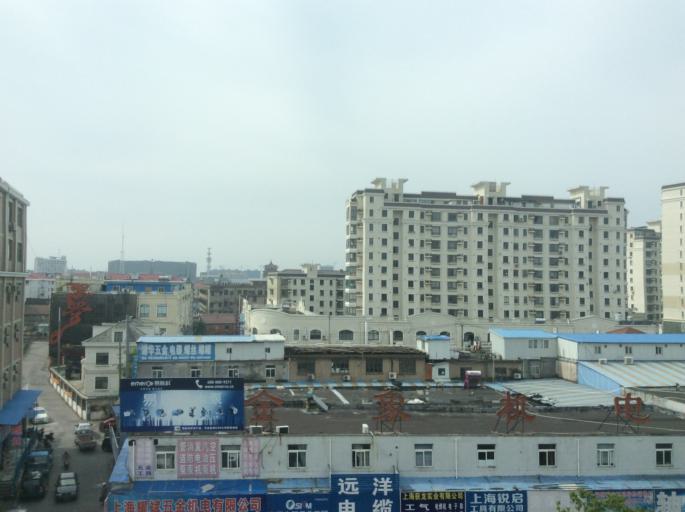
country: CN
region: Shanghai Shi
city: Kangqiao
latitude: 31.2020
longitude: 121.6950
